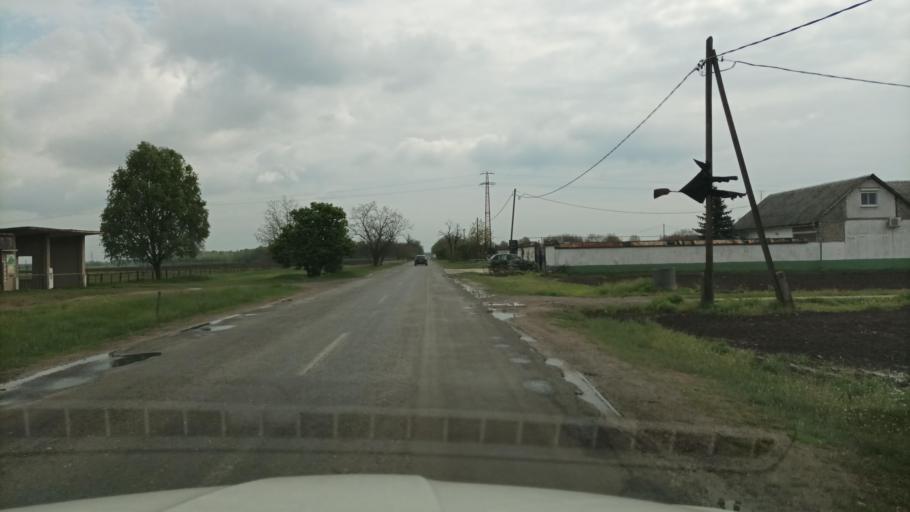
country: HU
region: Pest
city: Nagykoros
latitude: 47.0271
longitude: 19.8143
